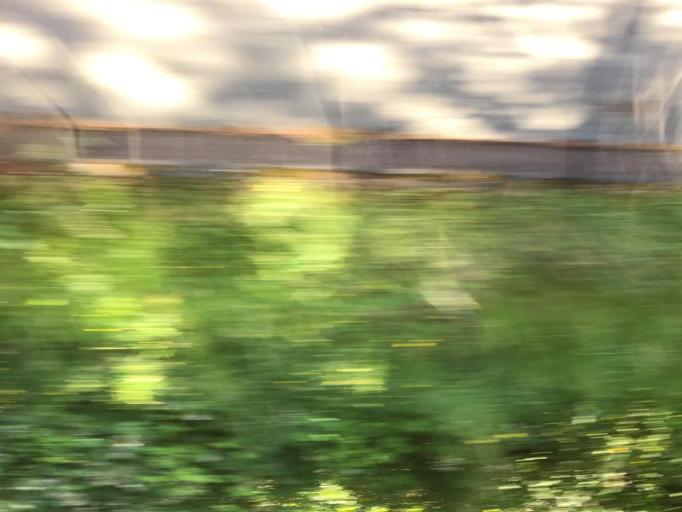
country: US
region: Washington
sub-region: King County
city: Redmond
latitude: 47.6417
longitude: -122.1185
